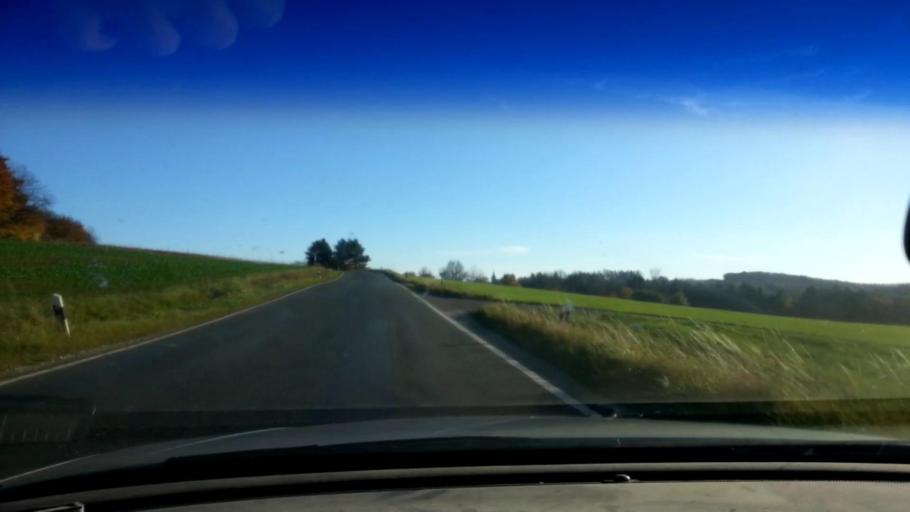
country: DE
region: Bavaria
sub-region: Upper Franconia
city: Poxdorf
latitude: 49.9155
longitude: 11.0890
